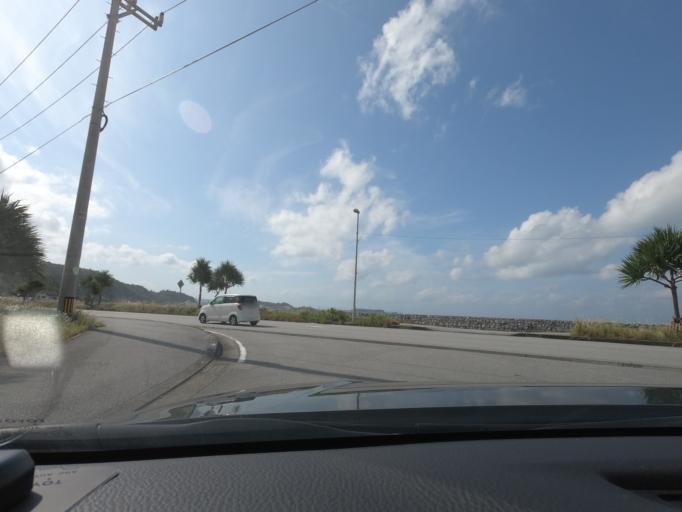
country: JP
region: Okinawa
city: Nago
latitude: 26.7551
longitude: 128.1883
